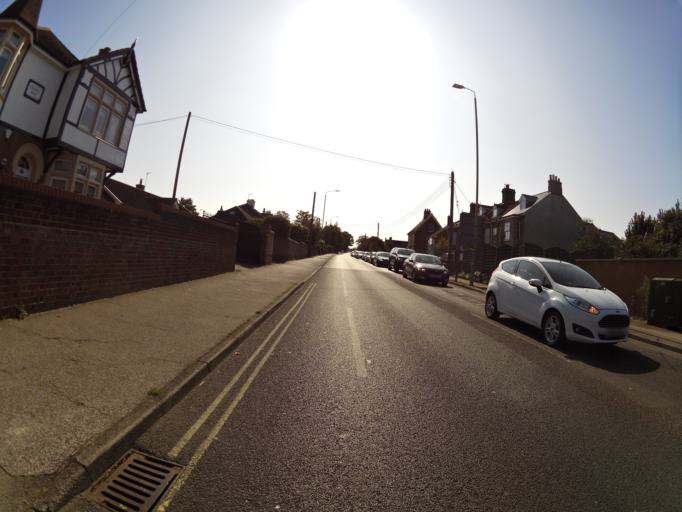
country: GB
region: England
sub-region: Suffolk
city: Lowestoft
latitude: 52.4685
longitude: 1.7072
